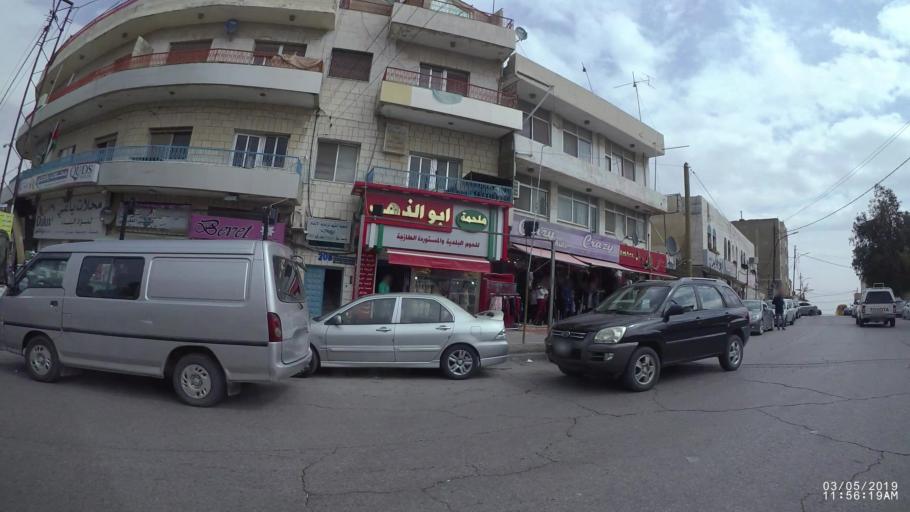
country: JO
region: Amman
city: Amman
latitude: 31.9707
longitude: 35.9293
